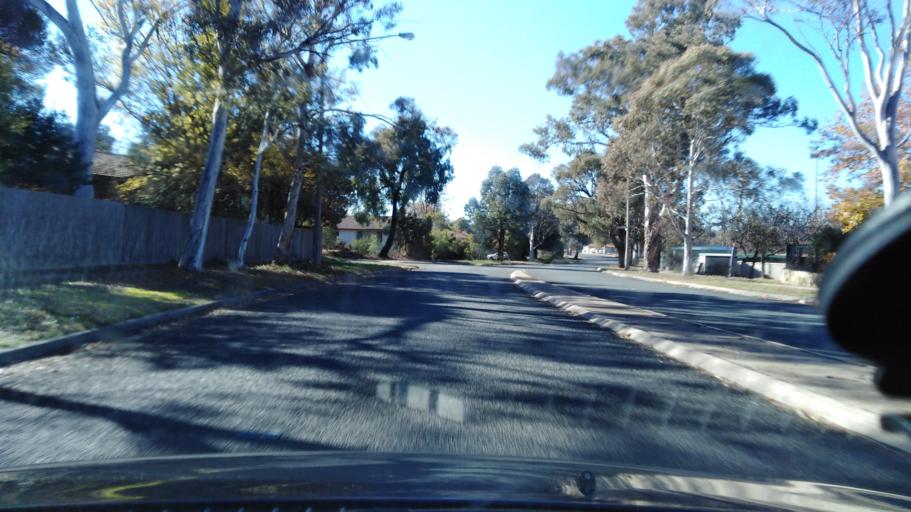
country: AU
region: Australian Capital Territory
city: Forrest
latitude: -35.3465
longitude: 149.0363
